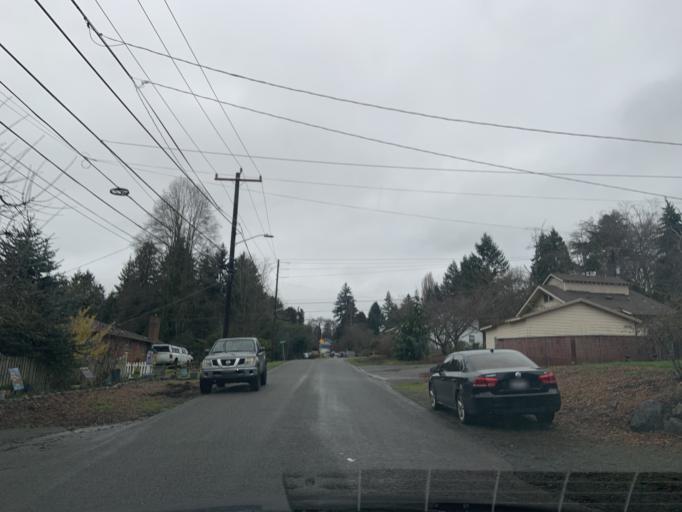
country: US
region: Washington
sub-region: King County
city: Lake Forest Park
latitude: 47.7112
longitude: -122.2880
